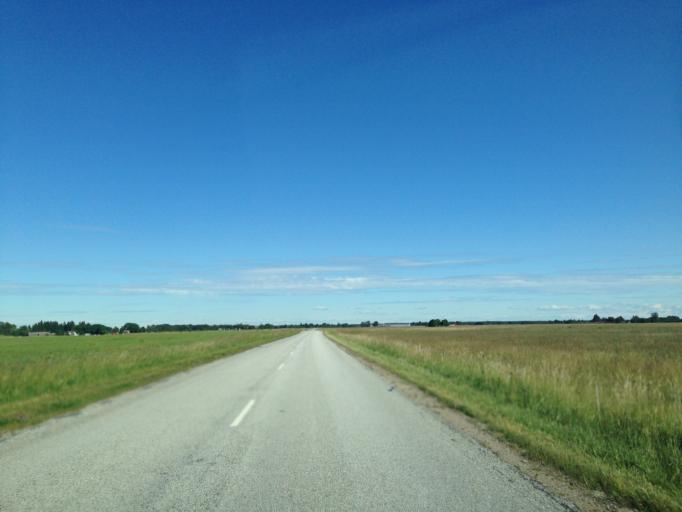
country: EE
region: Harju
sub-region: Kuusalu vald
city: Kuusalu
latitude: 59.4660
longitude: 25.3211
